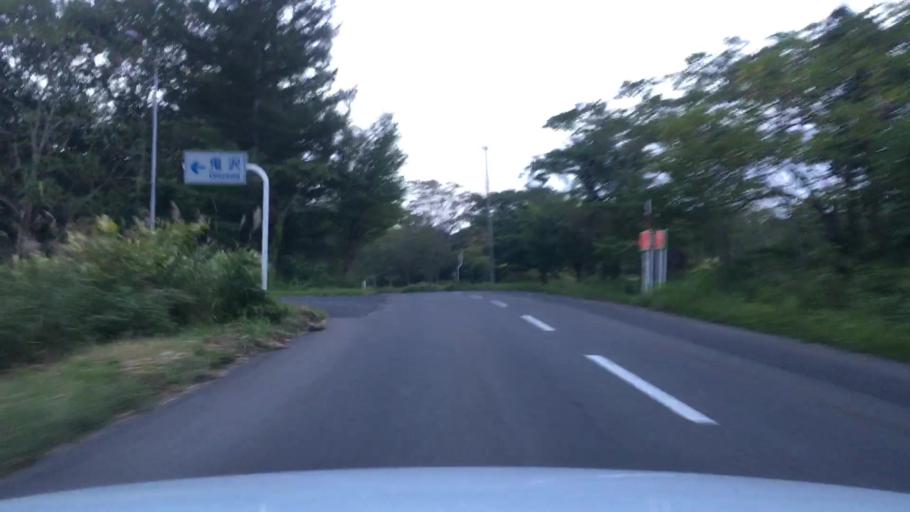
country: JP
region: Aomori
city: Shimokizukuri
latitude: 40.6885
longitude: 140.3628
